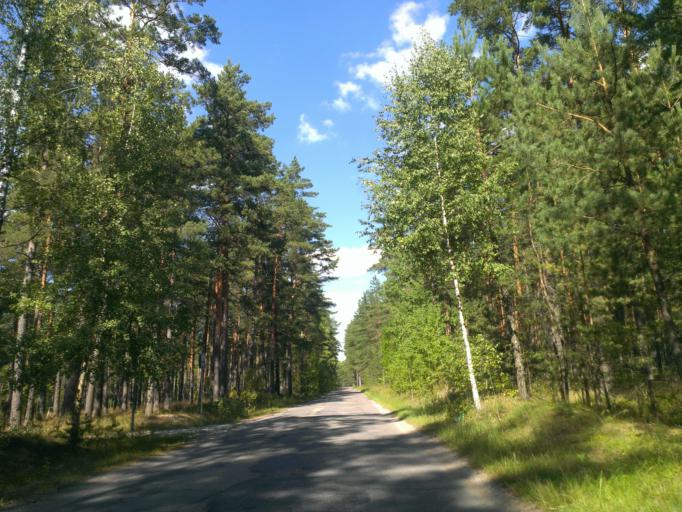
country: LV
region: Adazi
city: Adazi
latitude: 57.1185
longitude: 24.3455
